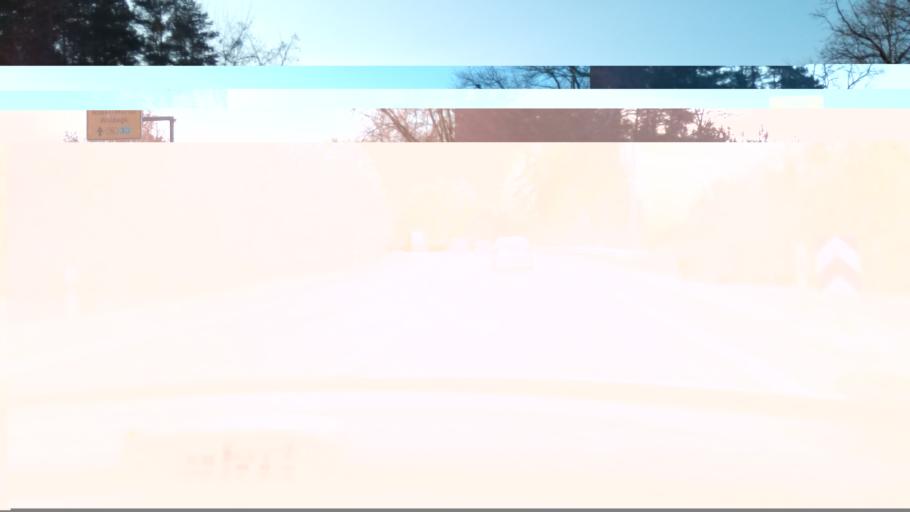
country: DE
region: Mecklenburg-Vorpommern
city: Neustrelitz
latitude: 53.3779
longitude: 13.0779
